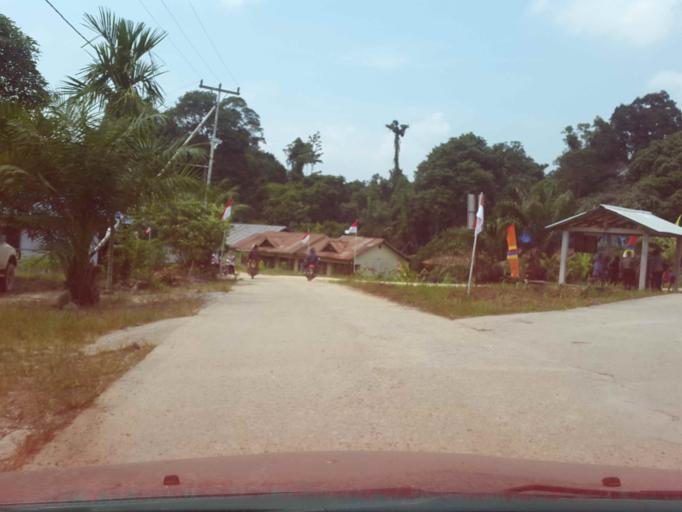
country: MY
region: Sarawak
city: Simanggang
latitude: 0.8409
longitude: 111.7465
